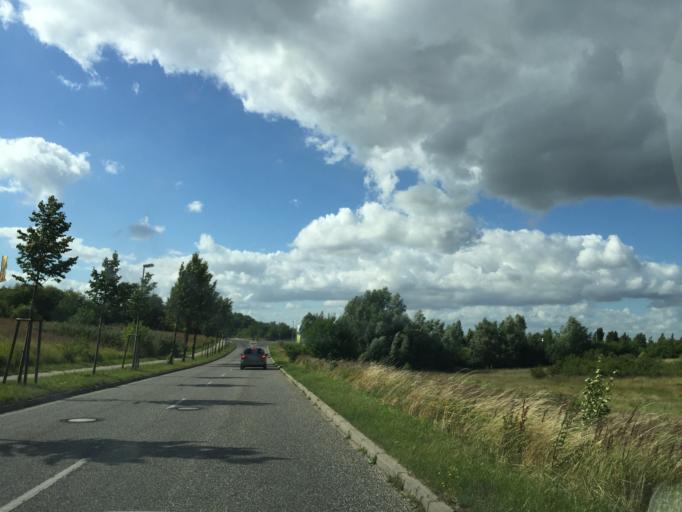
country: DE
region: Mecklenburg-Vorpommern
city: Neubrandenburg
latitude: 53.5253
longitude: 13.2697
